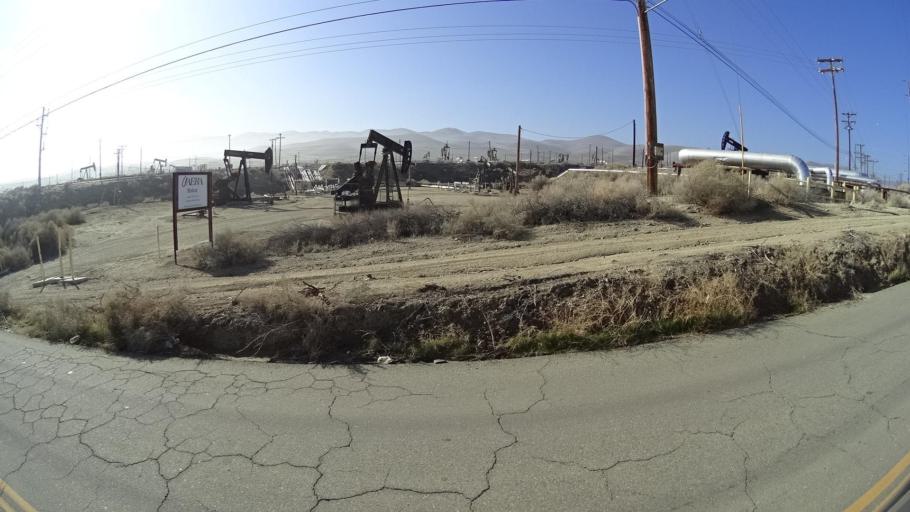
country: US
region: California
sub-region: Kern County
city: Taft Heights
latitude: 35.2243
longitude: -119.6231
